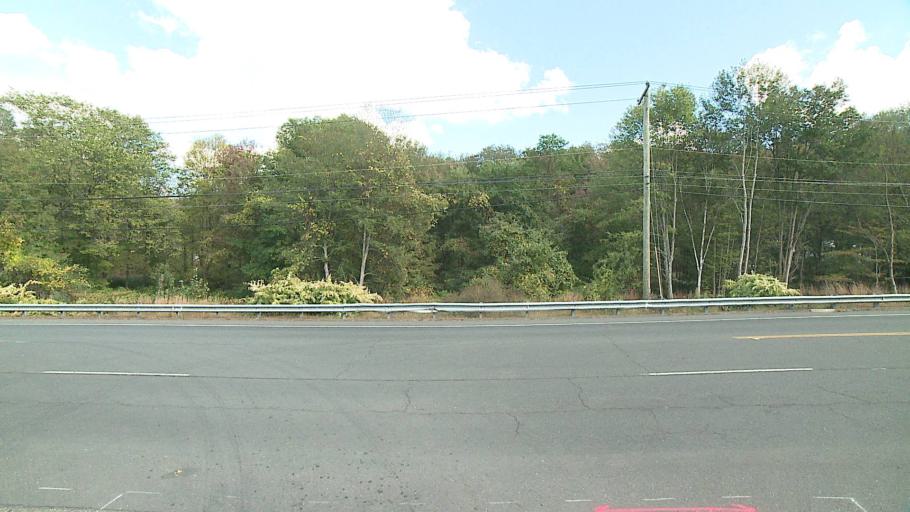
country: US
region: Connecticut
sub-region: New Haven County
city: Prospect
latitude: 41.4546
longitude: -72.9881
